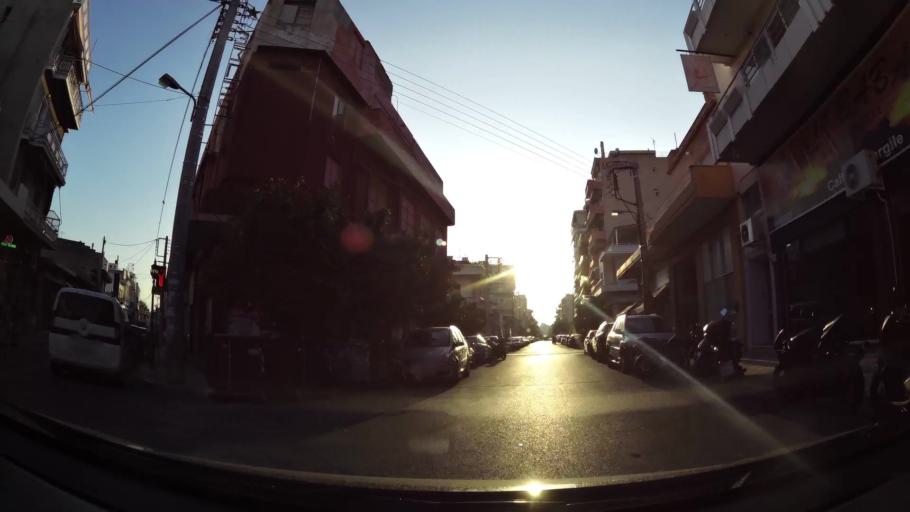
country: GR
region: Attica
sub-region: Nomos Piraios
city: Nikaia
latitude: 37.9677
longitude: 23.6508
